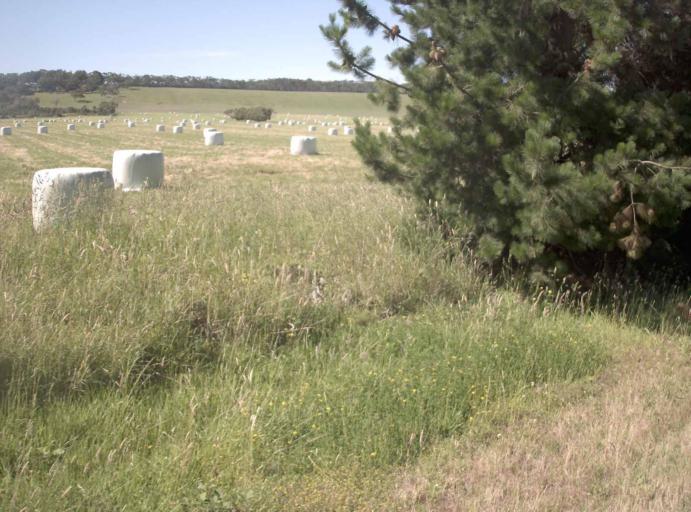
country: AU
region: Victoria
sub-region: Latrobe
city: Morwell
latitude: -38.6550
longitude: 146.4604
